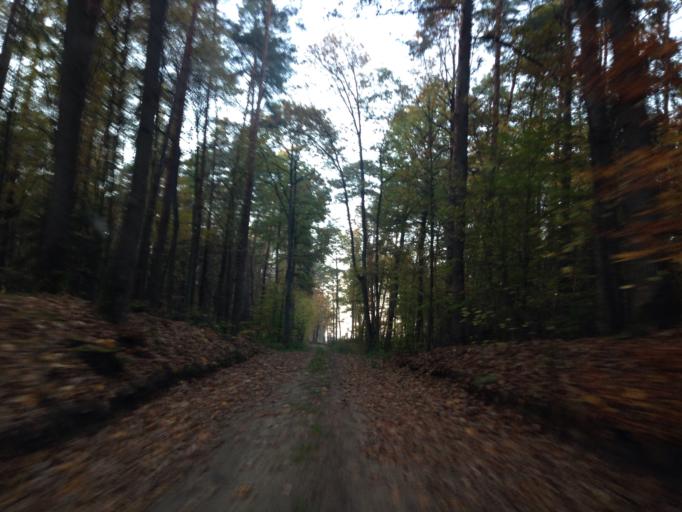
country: PL
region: Kujawsko-Pomorskie
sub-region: Powiat brodnicki
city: Gorzno
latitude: 53.2117
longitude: 19.7119
